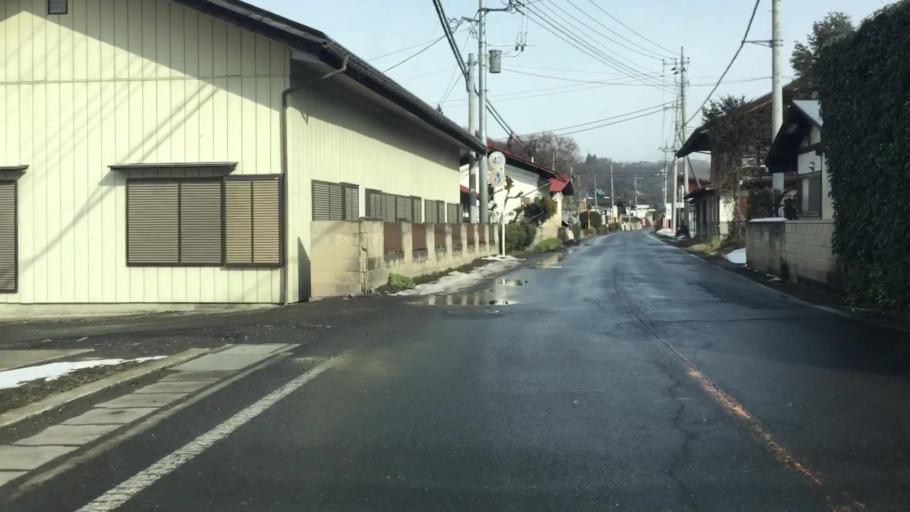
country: JP
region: Gunma
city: Numata
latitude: 36.6516
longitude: 139.0858
